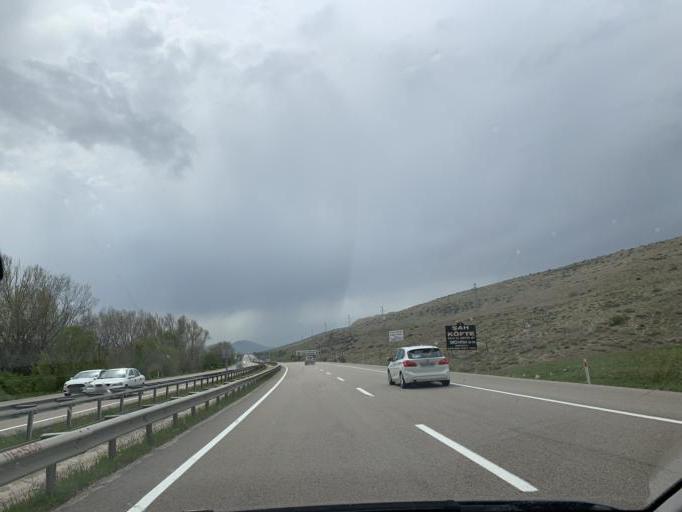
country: TR
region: Eskisehir
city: Gunyuzu
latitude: 39.5435
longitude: 31.7114
